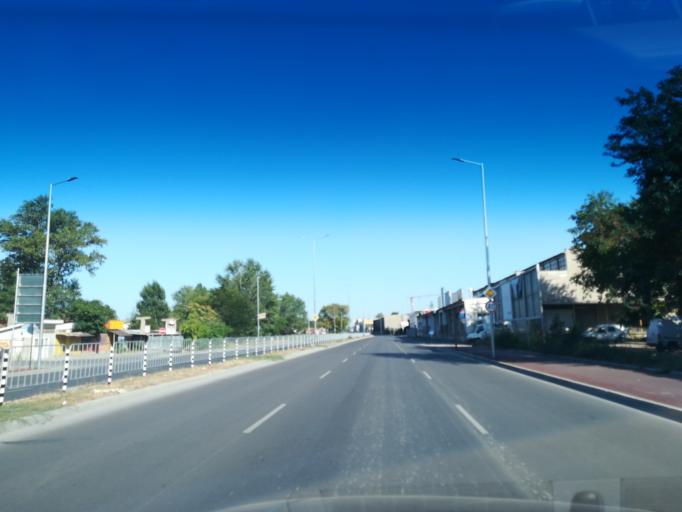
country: BG
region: Plovdiv
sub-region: Obshtina Plovdiv
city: Plovdiv
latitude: 42.1663
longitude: 24.7529
